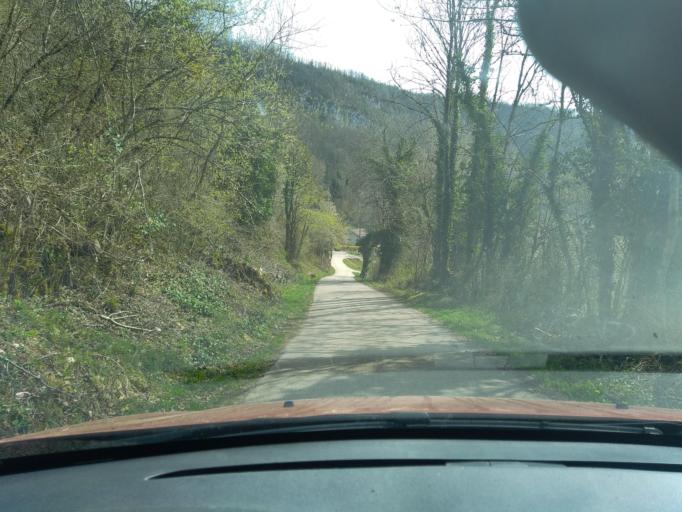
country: FR
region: Franche-Comte
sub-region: Departement du Jura
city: Moirans-en-Montagne
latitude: 46.4681
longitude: 5.7422
